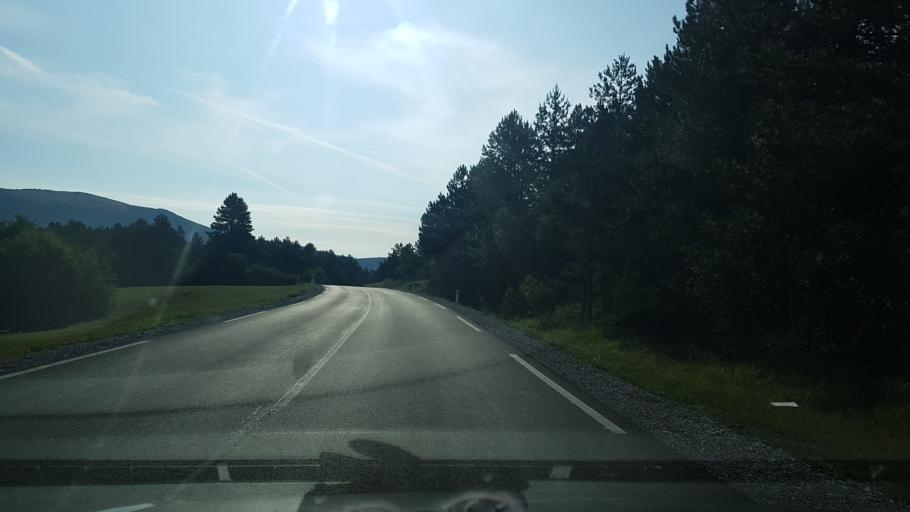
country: SI
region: Divaca
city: Divaca
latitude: 45.6788
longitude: 13.9933
